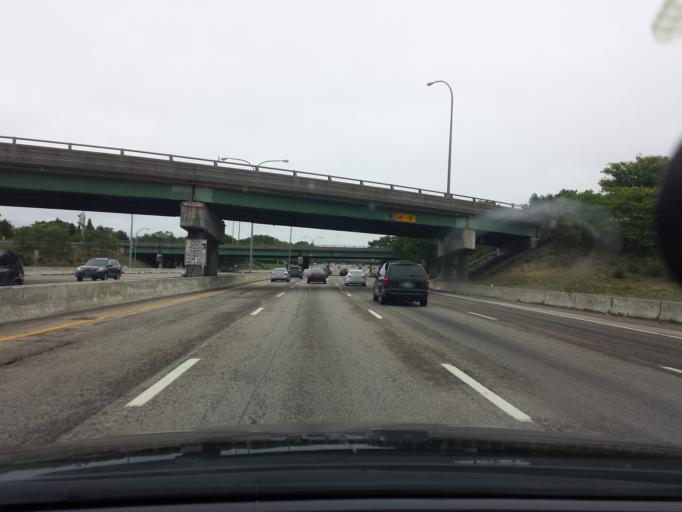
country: US
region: Rhode Island
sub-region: Providence County
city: Cranston
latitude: 41.7806
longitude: -71.4248
